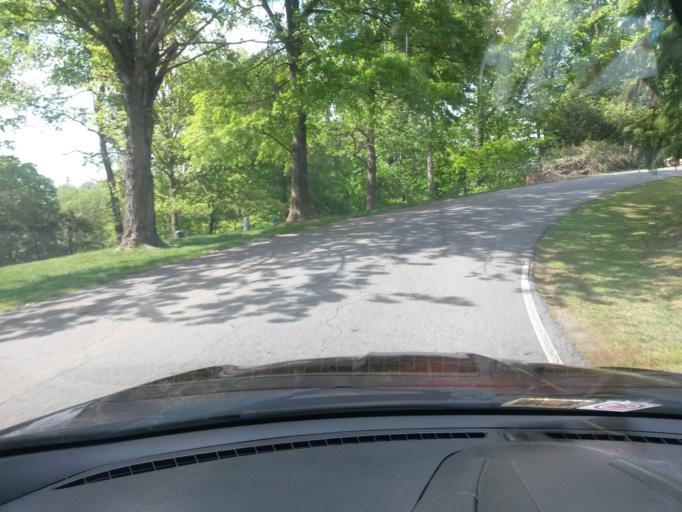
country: US
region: Virginia
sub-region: Campbell County
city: Timberlake
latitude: 37.3487
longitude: -79.2194
